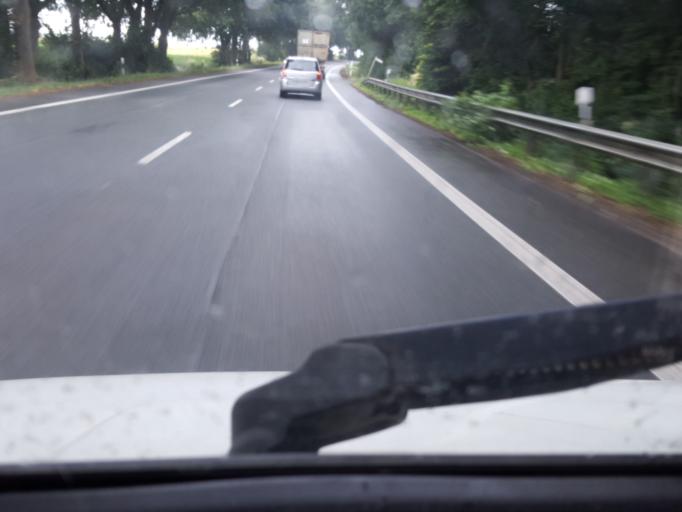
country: DE
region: North Rhine-Westphalia
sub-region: Regierungsbezirk Detmold
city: Minden
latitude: 52.3336
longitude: 8.9294
